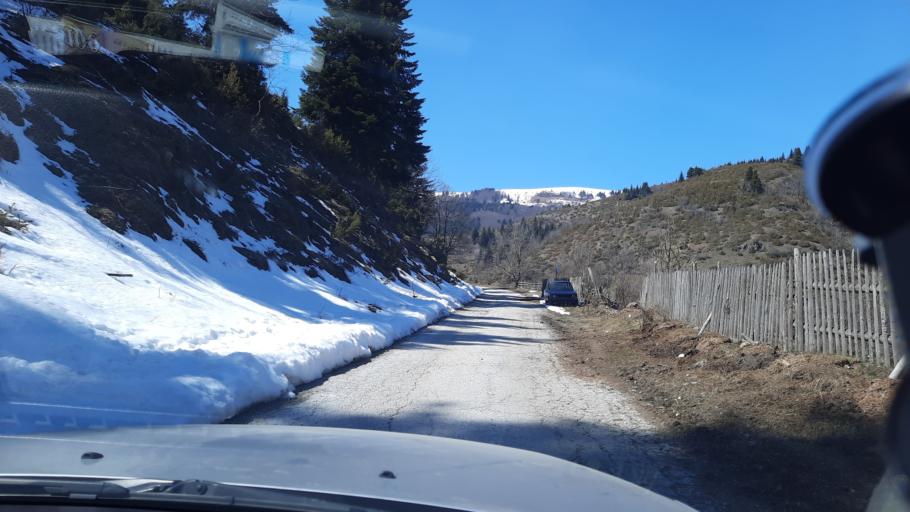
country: MK
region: Gostivar
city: Vrutok
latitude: 41.7199
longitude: 20.7330
